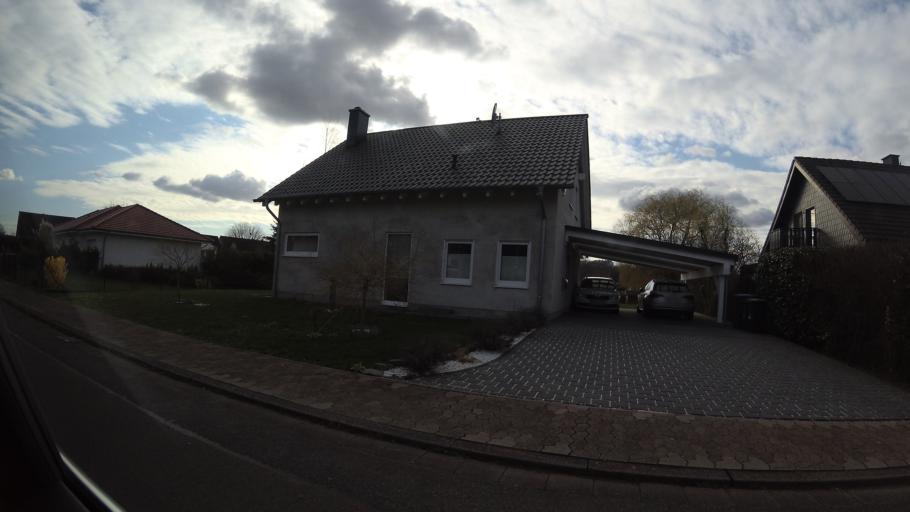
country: DE
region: Saarland
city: Blieskastel
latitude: 49.2292
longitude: 7.2710
